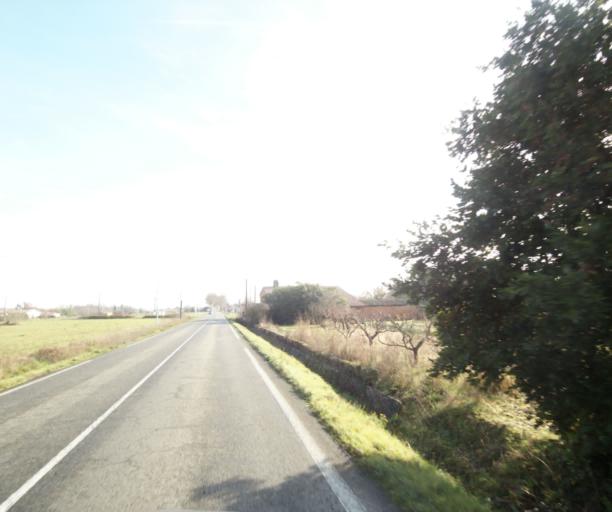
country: FR
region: Midi-Pyrenees
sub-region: Departement du Tarn-et-Garonne
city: Nohic
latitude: 43.8750
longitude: 1.4588
